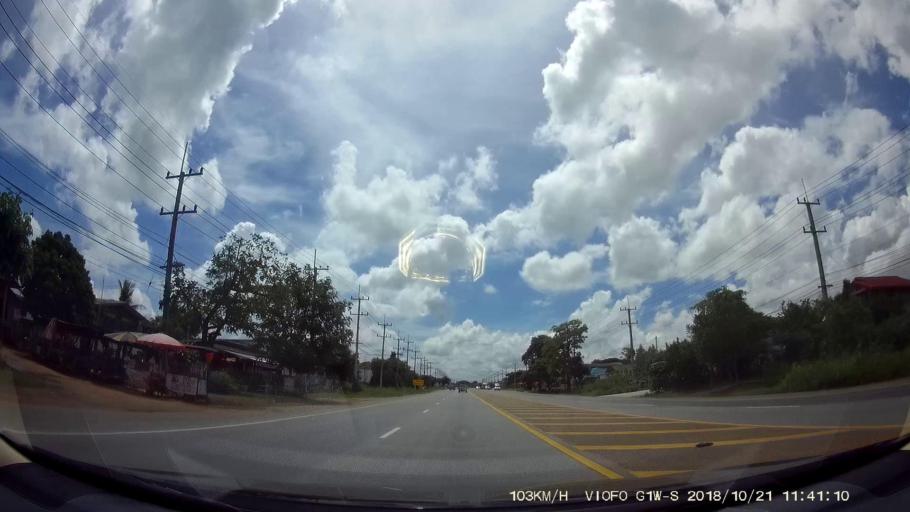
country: TH
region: Chaiyaphum
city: Chaiyaphum
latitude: 15.7031
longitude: 102.0149
